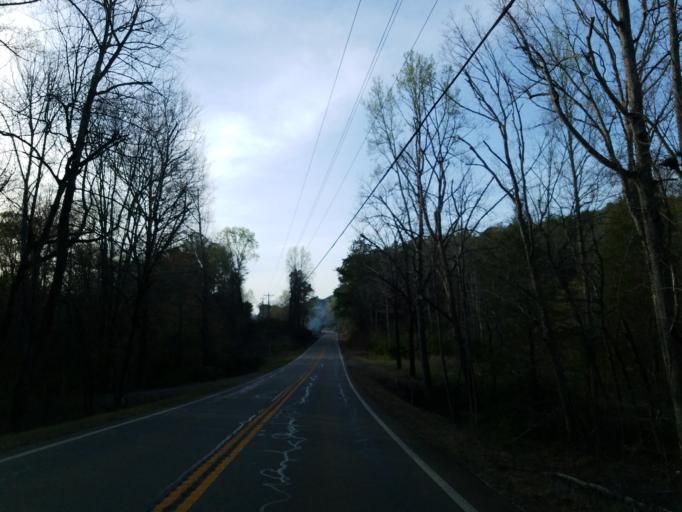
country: US
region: Georgia
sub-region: Pickens County
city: Jasper
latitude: 34.5196
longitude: -84.4674
